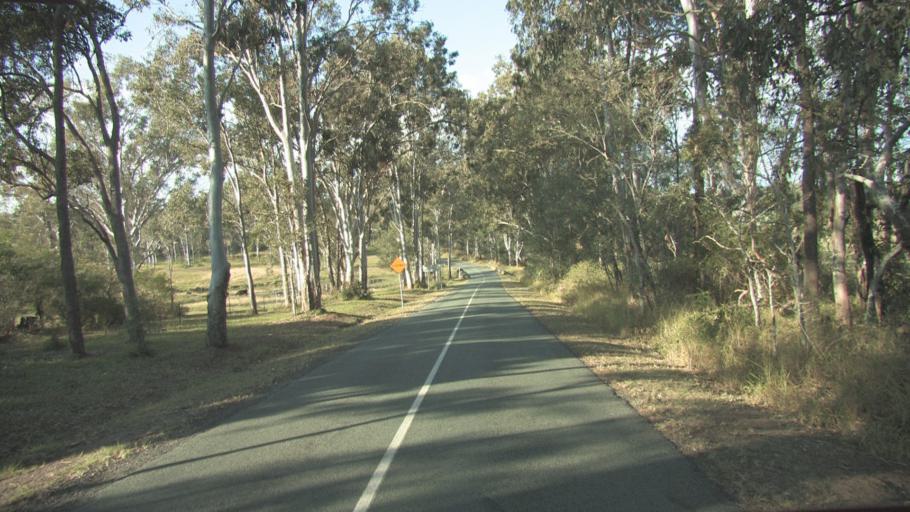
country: AU
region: Queensland
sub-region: Logan
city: Cedar Vale
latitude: -27.8498
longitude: 153.1362
